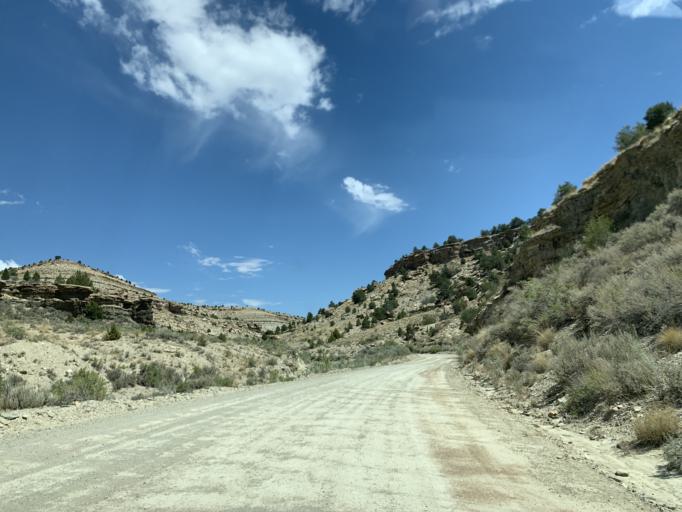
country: US
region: Utah
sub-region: Carbon County
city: East Carbon City
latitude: 39.8382
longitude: -110.2552
